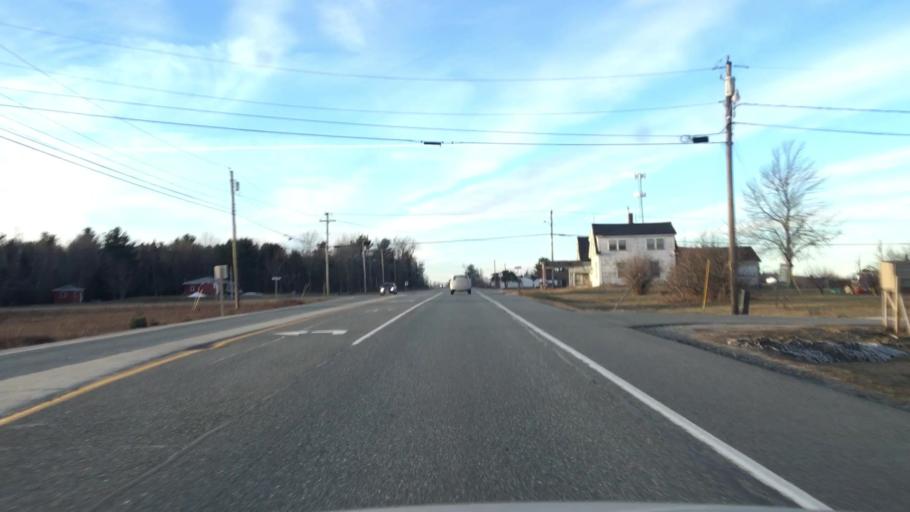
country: US
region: Maine
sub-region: Hancock County
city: Surry
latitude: 44.6150
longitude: -68.5245
